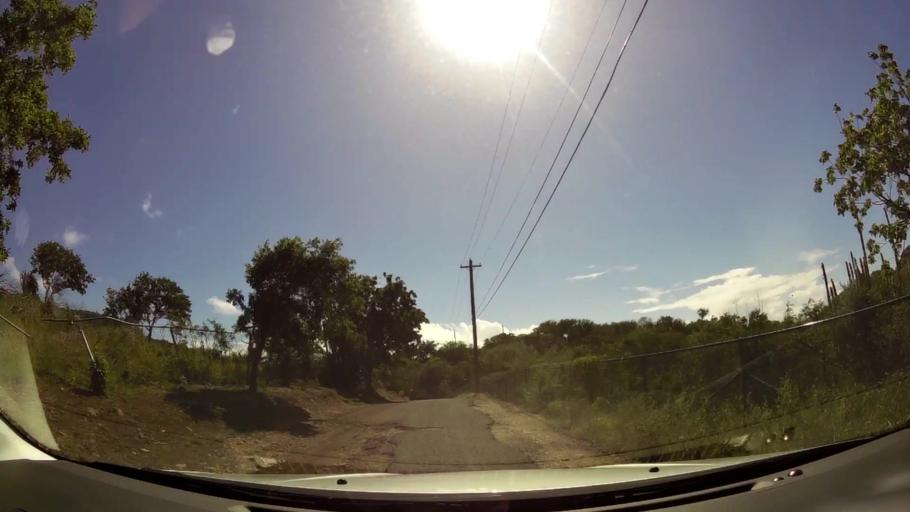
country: AG
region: Saint Paul
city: Falmouth
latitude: 17.0085
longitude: -61.7613
